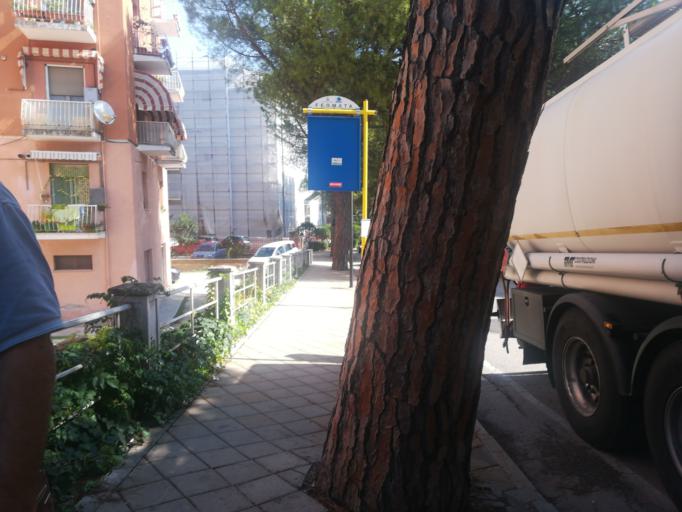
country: IT
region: The Marches
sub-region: Provincia di Macerata
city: Tolentino
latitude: 43.2115
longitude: 13.2873
